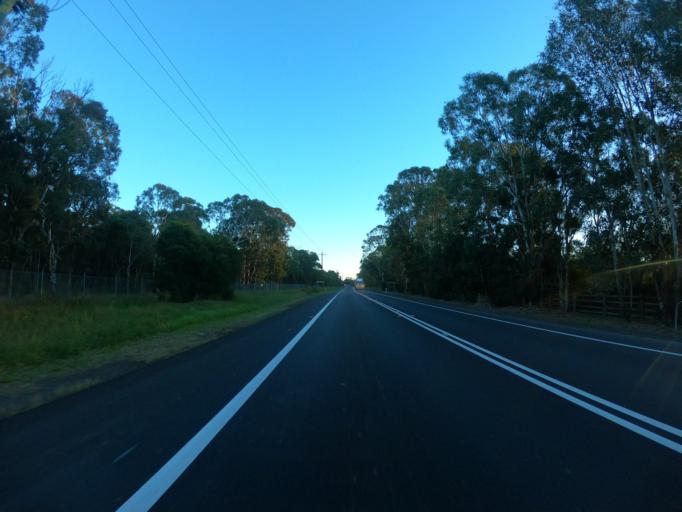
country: AU
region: New South Wales
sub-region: Hawkesbury
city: South Windsor
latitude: -33.6559
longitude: 150.7945
